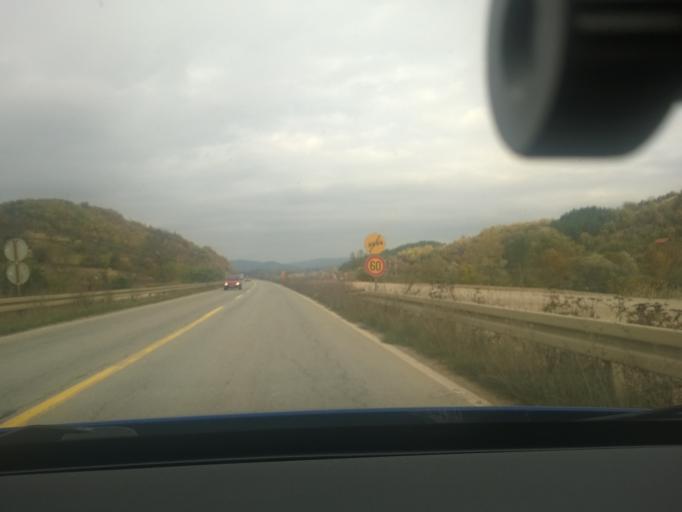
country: RS
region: Central Serbia
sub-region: Pirotski Okrug
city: Pirot
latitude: 43.1923
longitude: 22.5633
